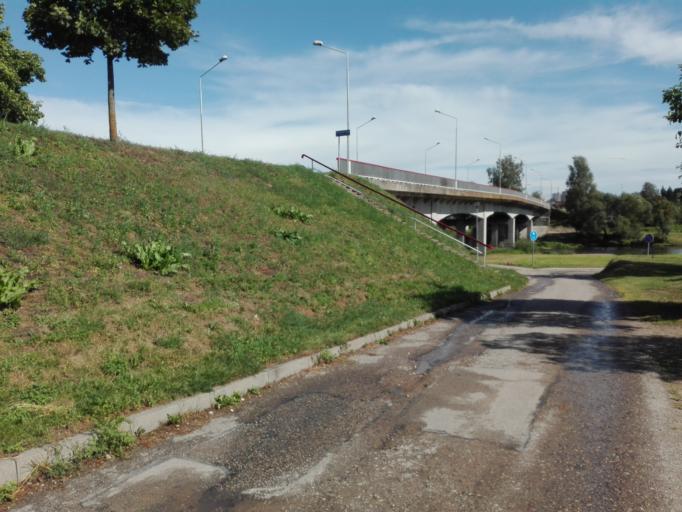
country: LT
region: Vilnius County
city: Ukmerge
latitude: 55.2474
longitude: 24.7676
